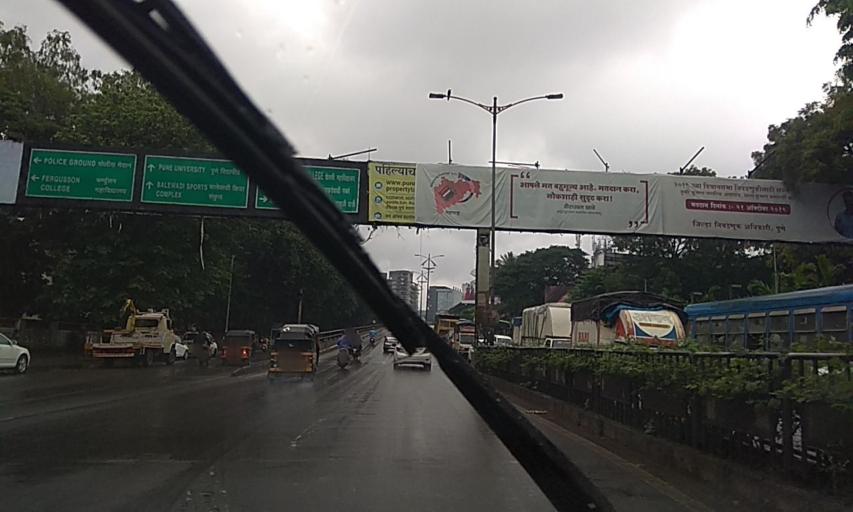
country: IN
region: Maharashtra
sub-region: Pune Division
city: Shivaji Nagar
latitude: 18.5308
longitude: 73.8471
